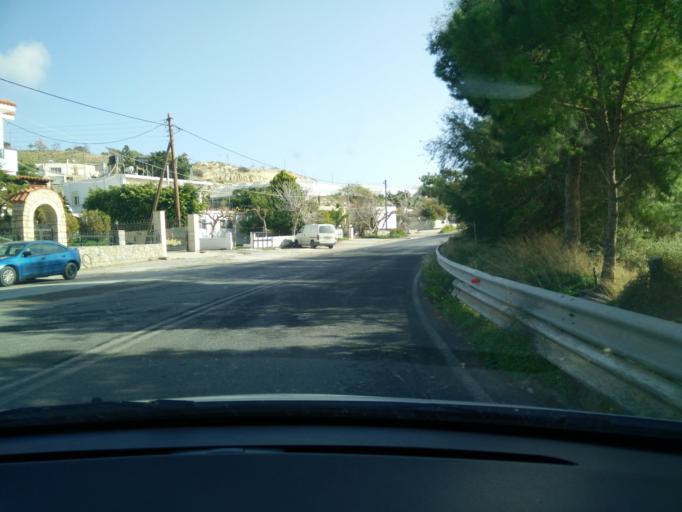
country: GR
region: Crete
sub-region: Nomos Lasithiou
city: Gra Liyia
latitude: 35.0090
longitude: 25.6326
